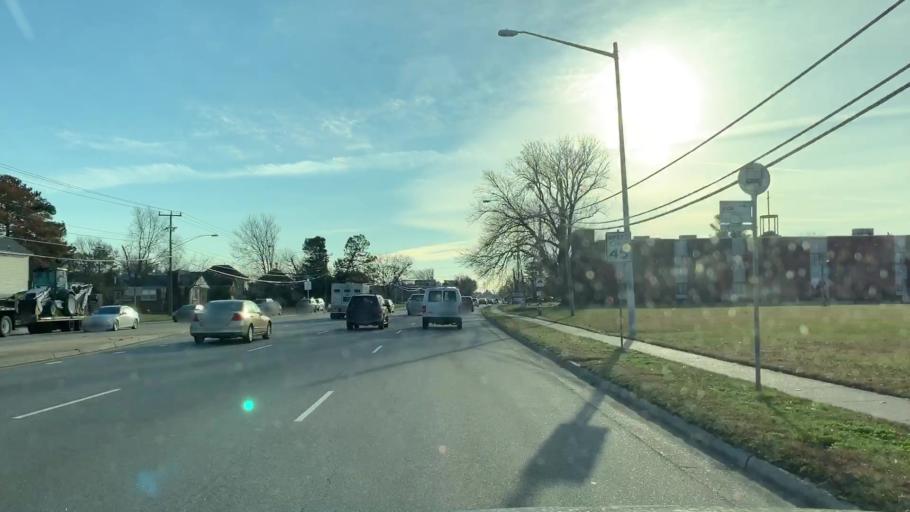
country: US
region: Virginia
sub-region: City of Chesapeake
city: Chesapeake
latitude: 36.8028
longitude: -76.1860
